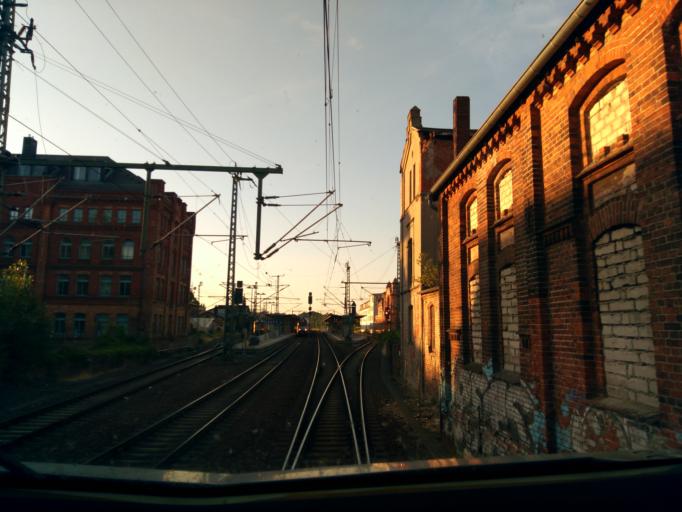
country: DE
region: Mecklenburg-Vorpommern
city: Paulsstadt
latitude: 53.6330
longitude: 11.4075
